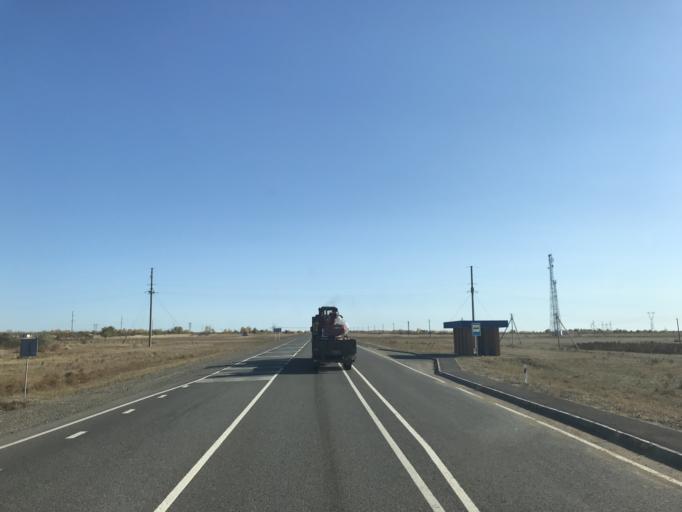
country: KZ
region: Pavlodar
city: Koktobe
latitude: 51.9245
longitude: 77.3364
